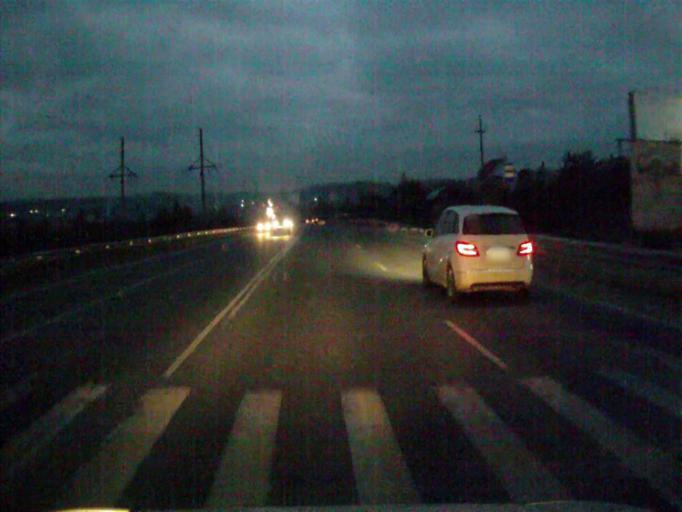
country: RU
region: Chelyabinsk
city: Sargazy
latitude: 55.1422
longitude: 61.2646
